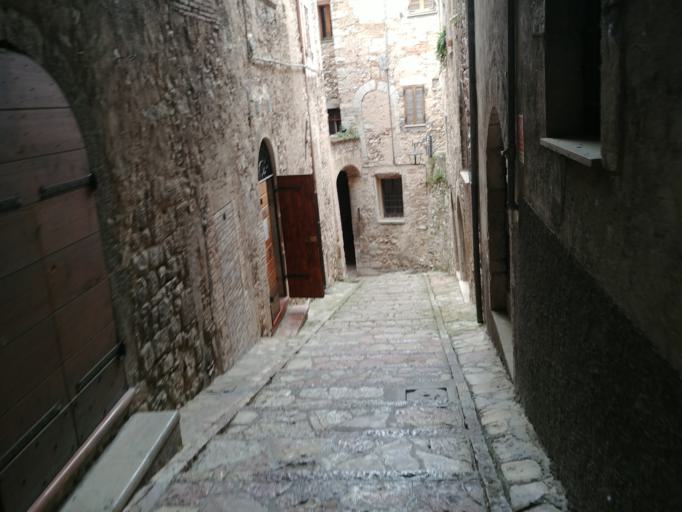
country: IT
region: Umbria
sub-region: Provincia di Terni
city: Stroncone
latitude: 42.4981
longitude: 12.6626
